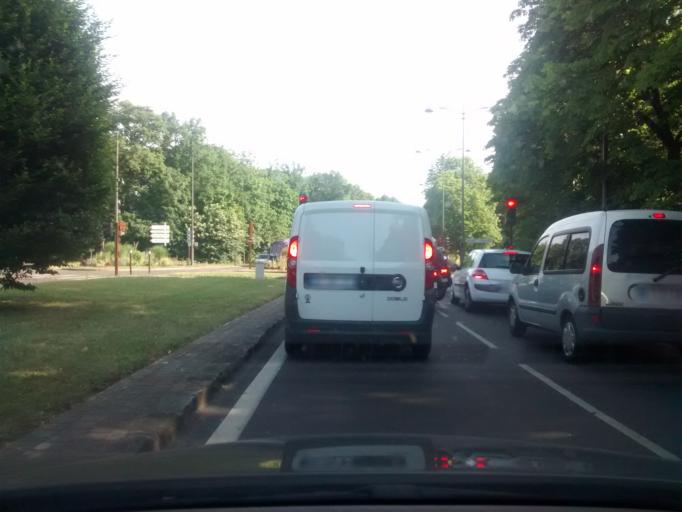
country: FR
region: Ile-de-France
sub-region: Departement des Yvelines
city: Viroflay
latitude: 48.8185
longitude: 2.1504
